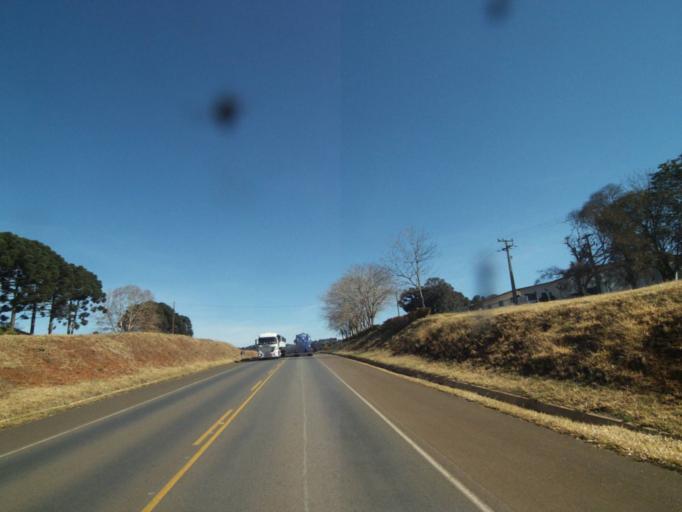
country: BR
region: Parana
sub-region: Tibagi
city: Tibagi
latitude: -24.4701
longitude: -50.4433
